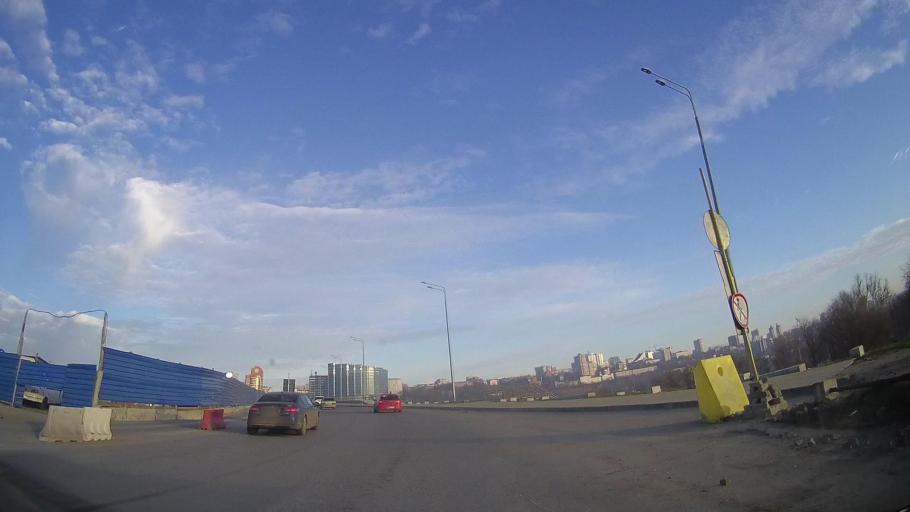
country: RU
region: Rostov
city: Rostov-na-Donu
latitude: 47.2107
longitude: 39.7247
